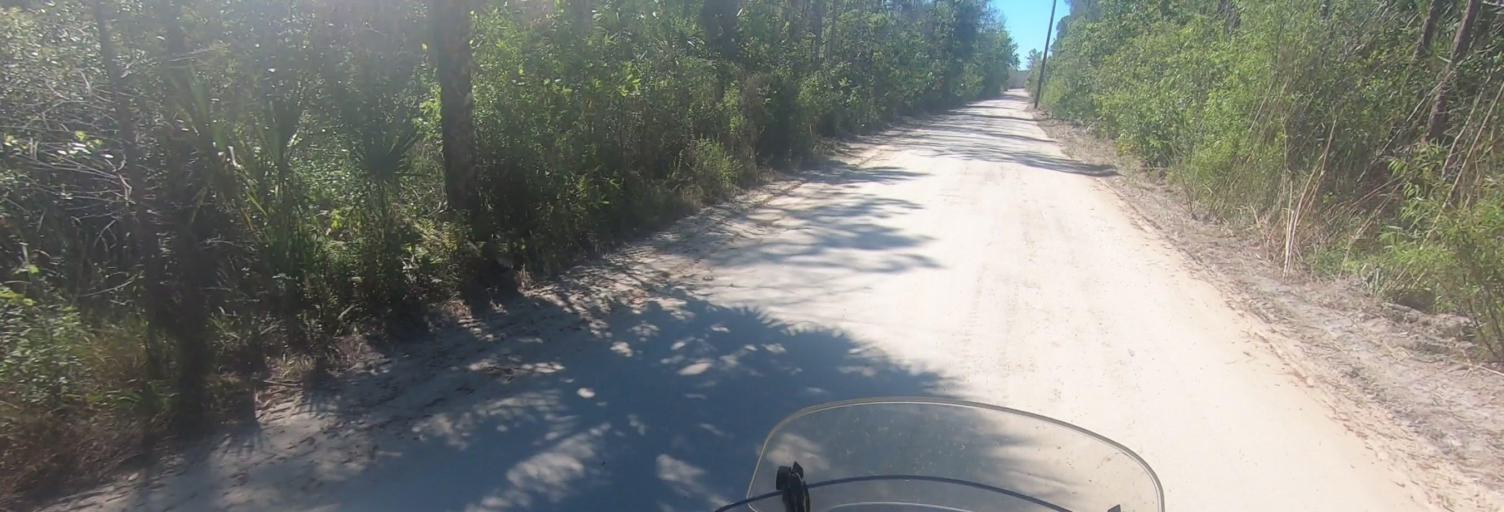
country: US
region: Florida
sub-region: Collier County
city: Lely Resort
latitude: 25.8891
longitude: -81.2299
